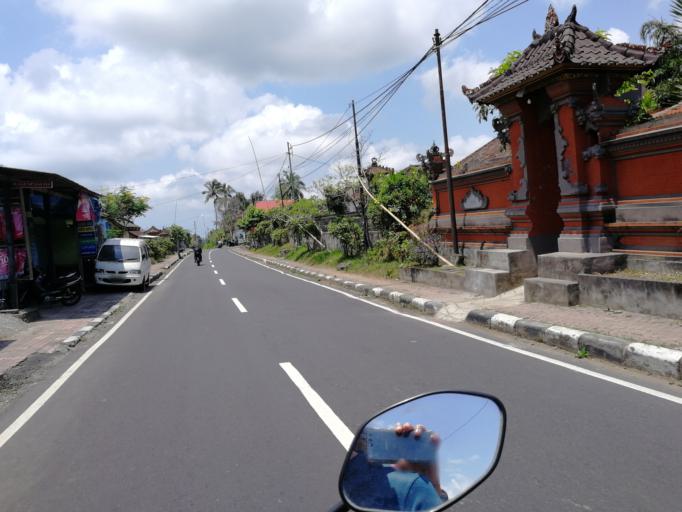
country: ID
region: Bali
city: Bangli
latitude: -8.4510
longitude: 115.3862
